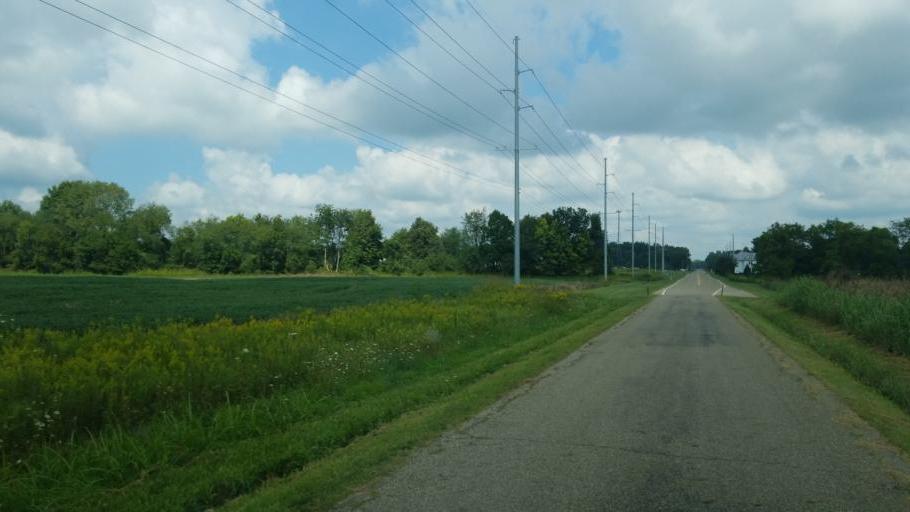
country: US
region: Ohio
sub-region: Knox County
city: Mount Vernon
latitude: 40.3436
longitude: -82.4850
